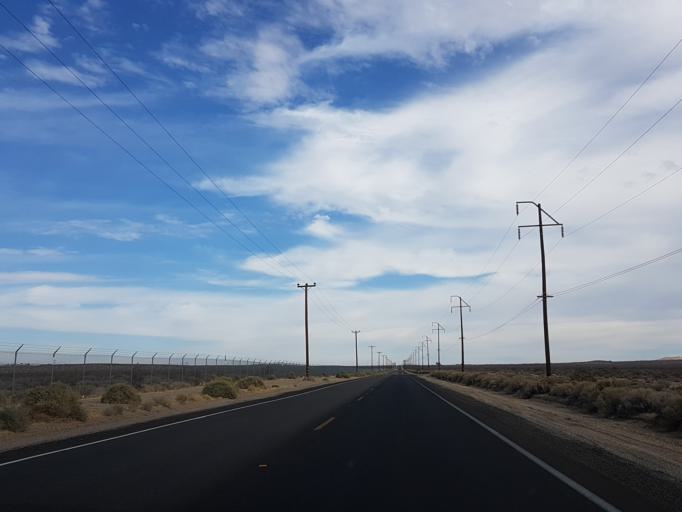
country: US
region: California
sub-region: Kern County
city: Ridgecrest
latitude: 35.6226
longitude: -117.6281
